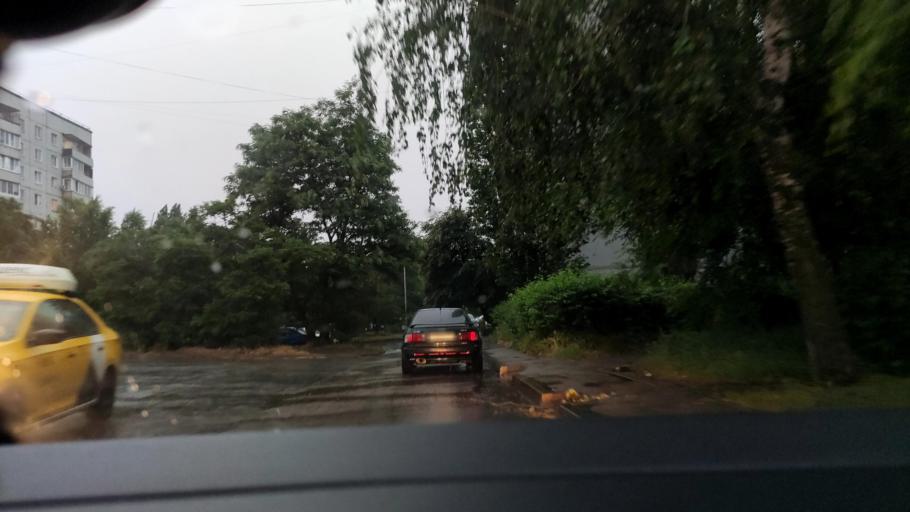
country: RU
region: Voronezj
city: Shilovo
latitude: 51.5522
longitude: 39.0915
